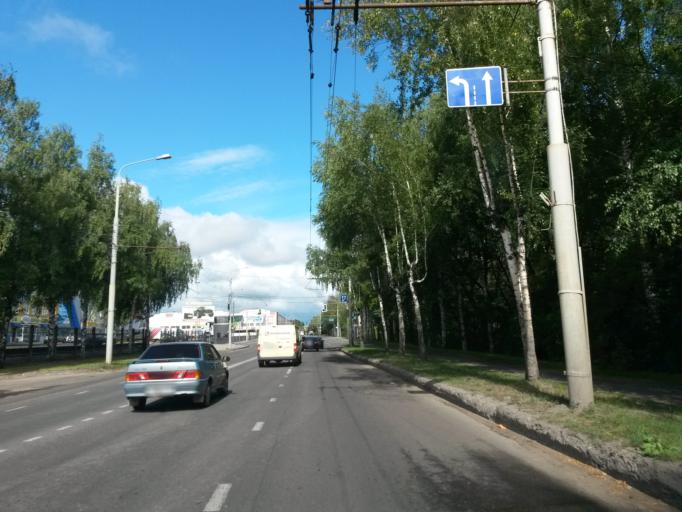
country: RU
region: Jaroslavl
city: Yaroslavl
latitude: 57.6540
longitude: 39.8712
